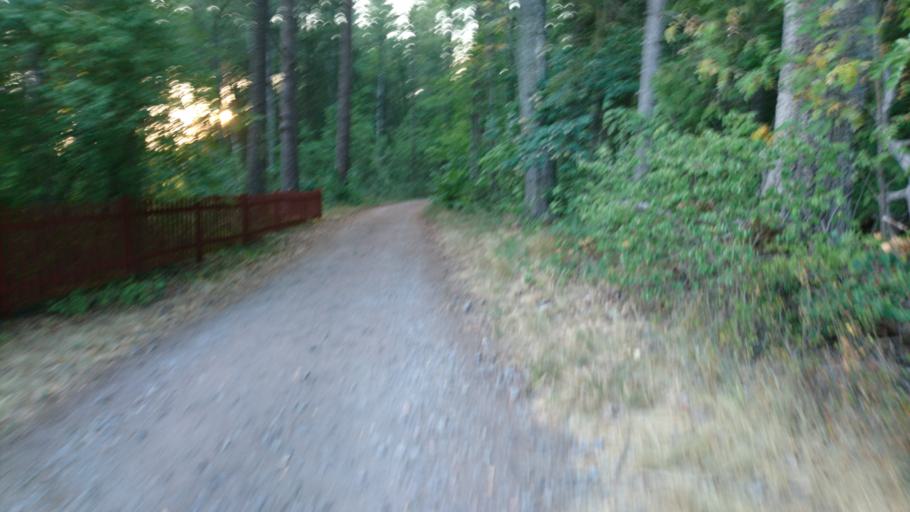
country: SE
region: Uppsala
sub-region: Uppsala Kommun
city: Saevja
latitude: 59.7711
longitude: 17.6521
